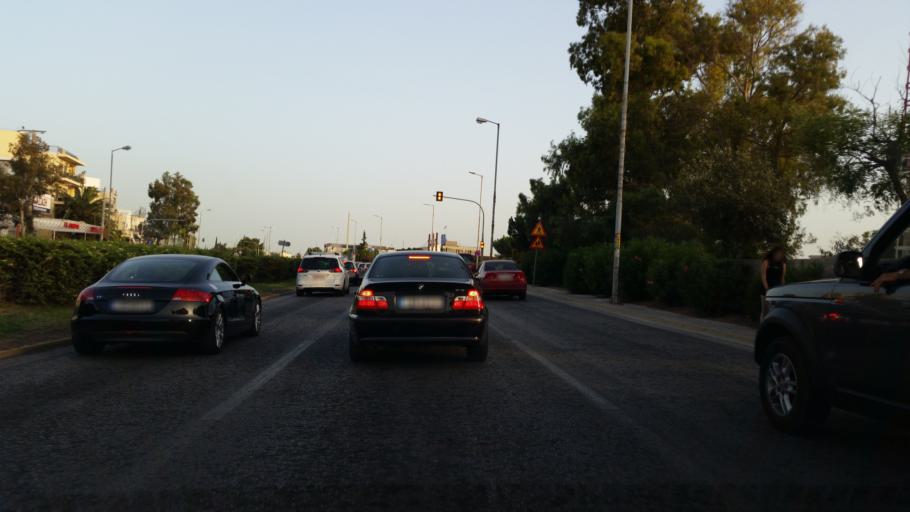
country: GR
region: Attica
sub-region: Nomarchia Athinas
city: Argyroupoli
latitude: 37.8939
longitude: 23.7470
